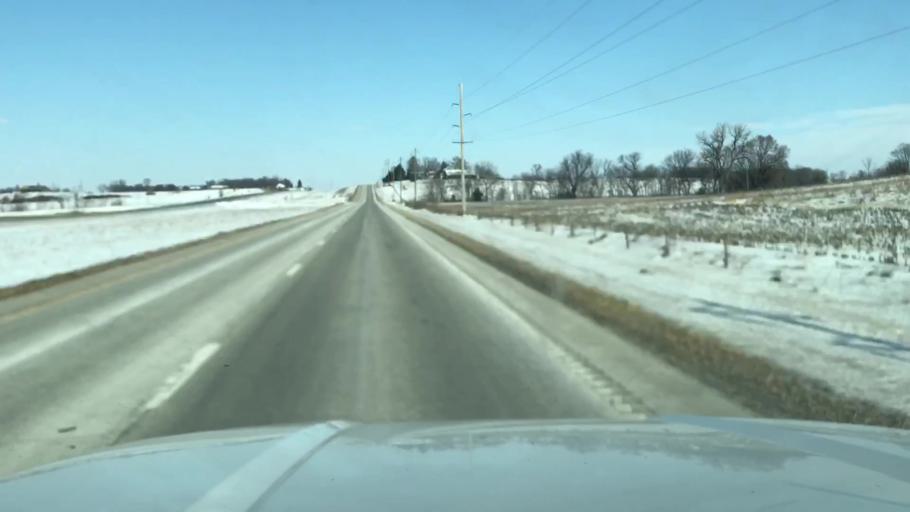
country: US
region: Missouri
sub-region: Nodaway County
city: Maryville
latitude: 40.1468
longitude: -94.8692
